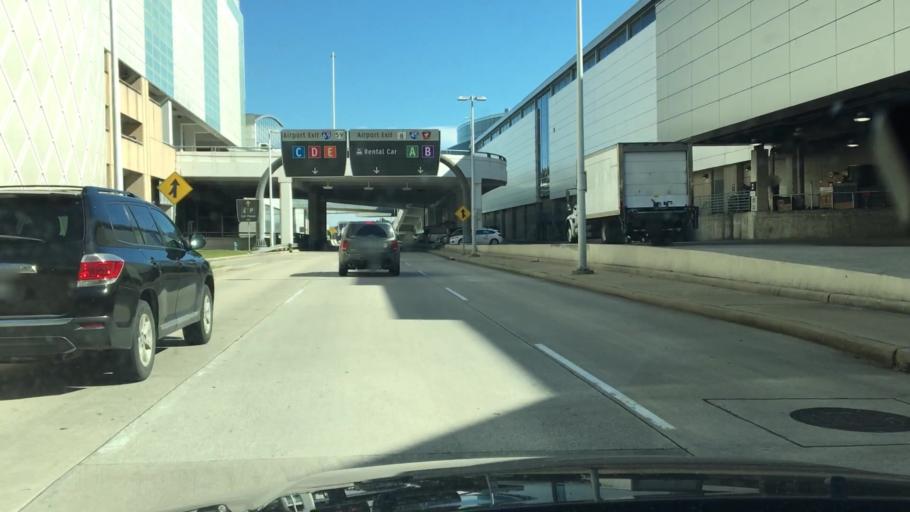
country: US
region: Texas
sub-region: Harris County
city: Aldine
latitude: 29.9860
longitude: -95.3355
